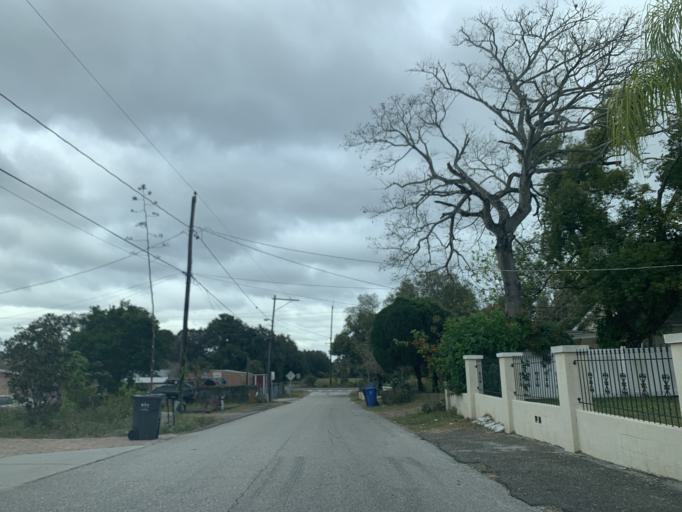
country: US
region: Florida
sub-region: Hillsborough County
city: East Lake-Orient Park
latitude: 27.9804
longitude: -82.3912
